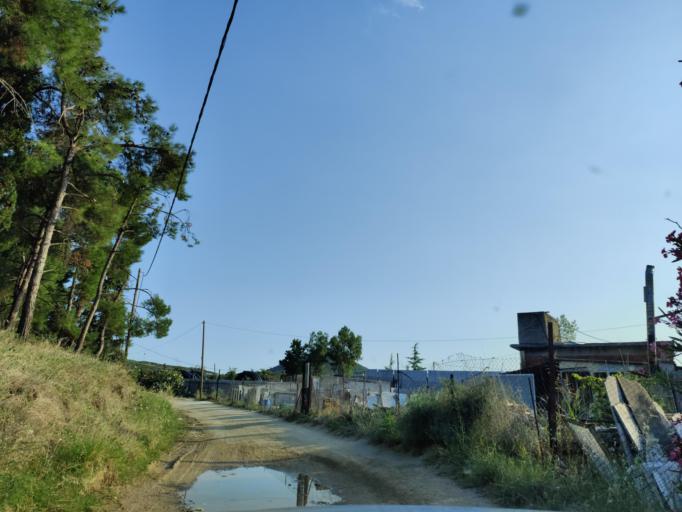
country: GR
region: East Macedonia and Thrace
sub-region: Nomos Kavalas
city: Nea Peramos
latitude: 40.8292
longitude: 24.2960
